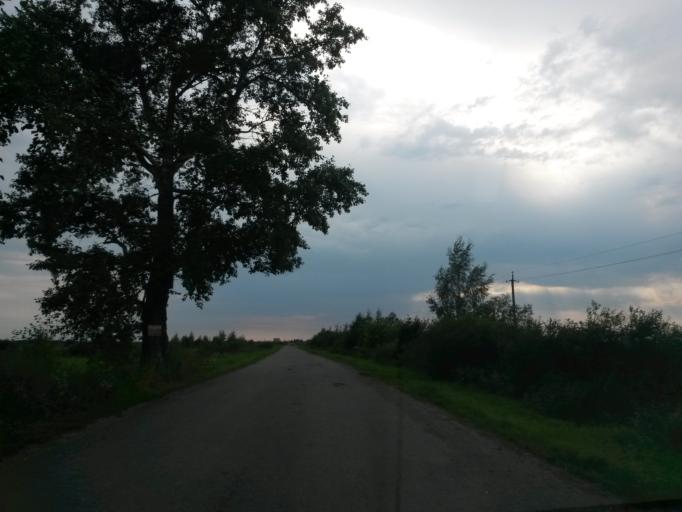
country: RU
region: Jaroslavl
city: Krasnyye Tkachi
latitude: 57.6039
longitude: 39.7523
